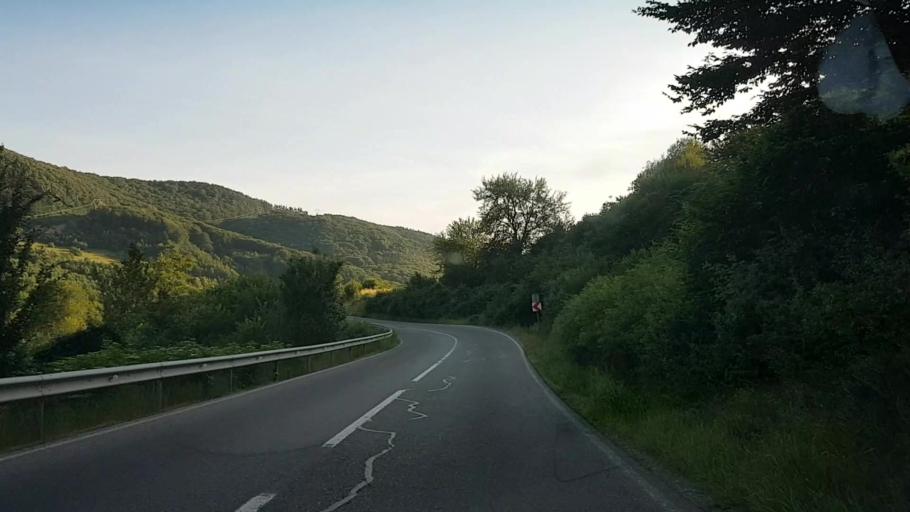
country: RO
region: Harghita
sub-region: Comuna Praid
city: Praid
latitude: 46.5659
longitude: 25.1602
